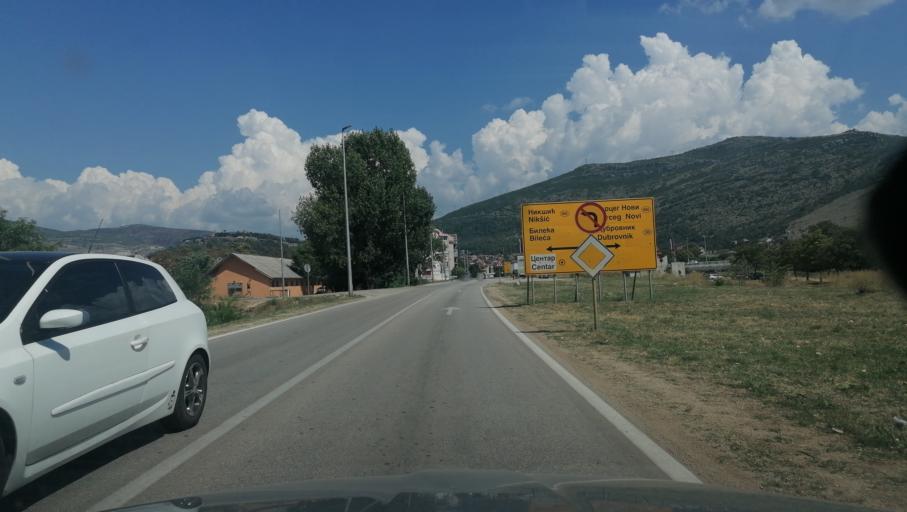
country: BA
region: Republika Srpska
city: Trebinje
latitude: 42.7055
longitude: 18.3406
